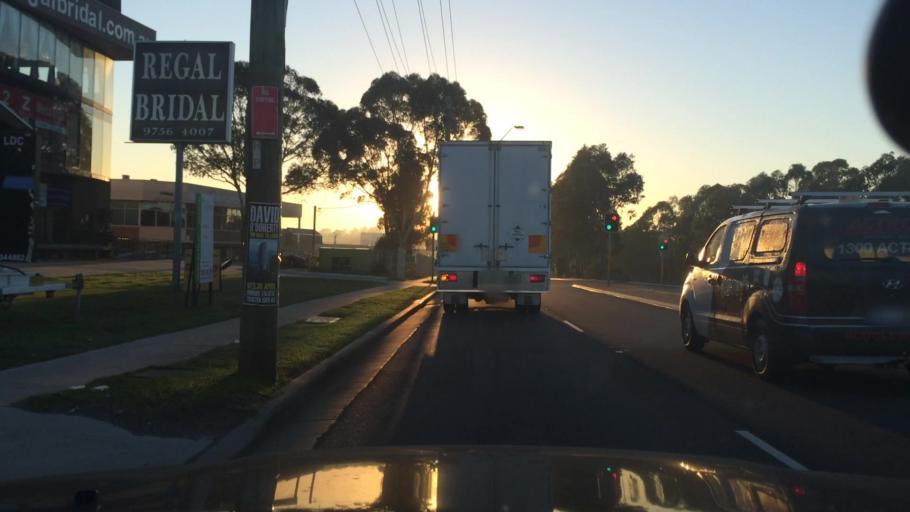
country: AU
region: New South Wales
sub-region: Fairfield
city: Horsley Park
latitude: -33.8523
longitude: 150.8919
